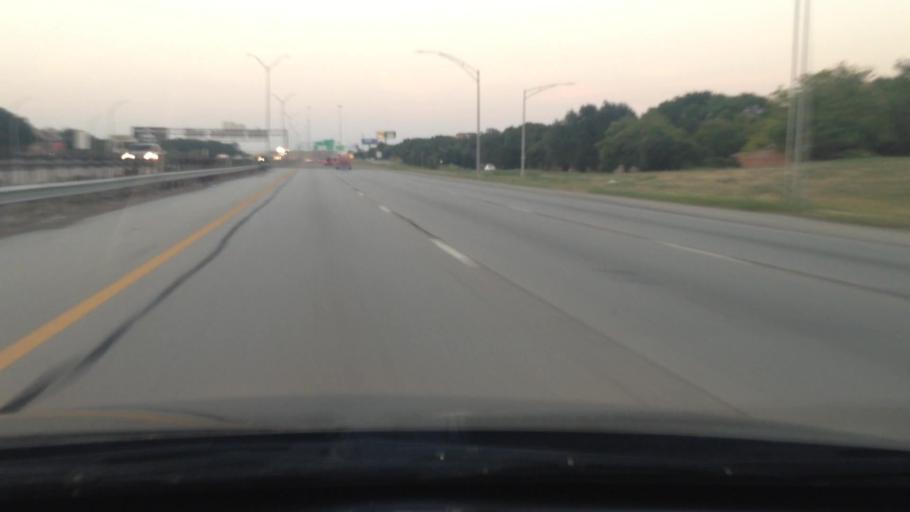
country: US
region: Texas
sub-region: Tarrant County
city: Richland Hills
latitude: 32.7467
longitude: -97.2219
